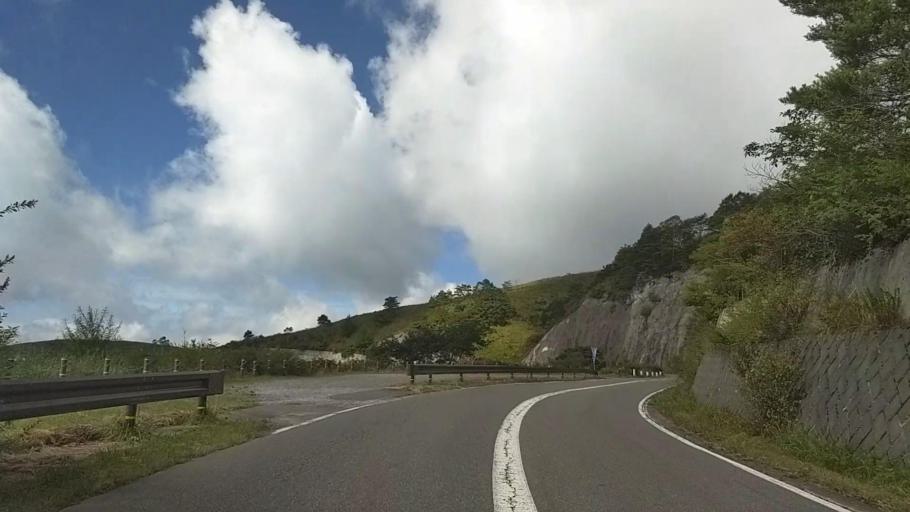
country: JP
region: Nagano
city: Suwa
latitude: 36.0946
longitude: 138.1955
